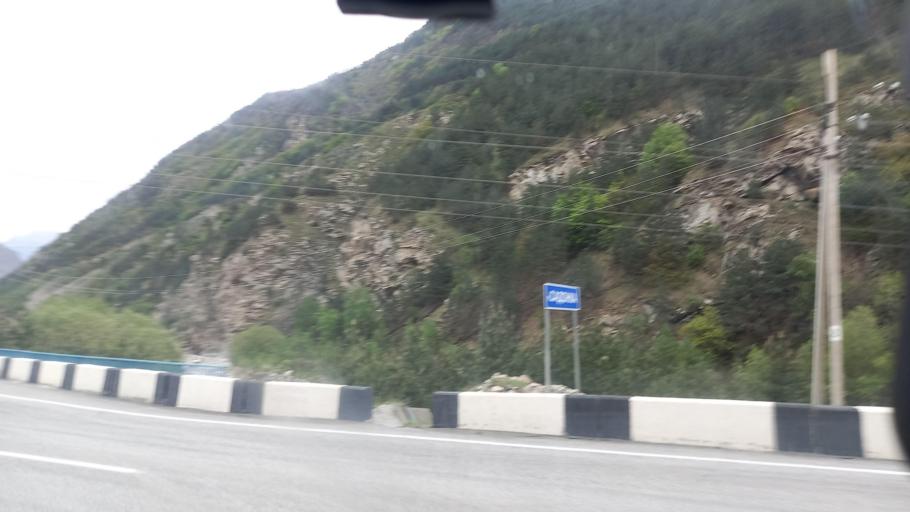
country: RU
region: North Ossetia
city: Mizur
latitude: 42.8389
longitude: 44.0280
